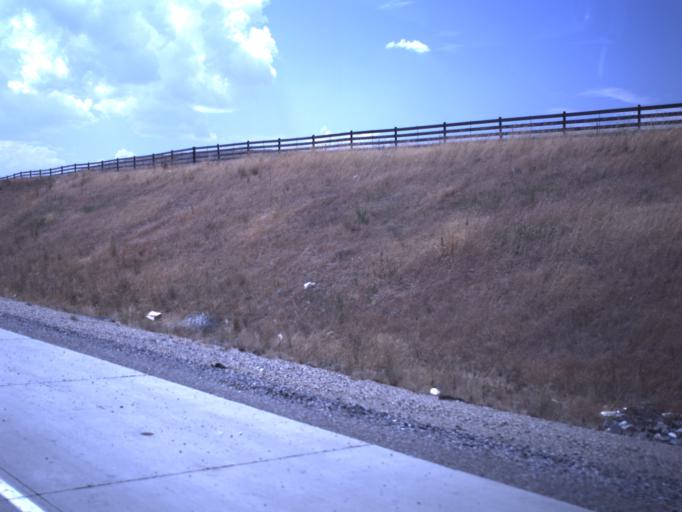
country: US
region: Utah
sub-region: Salt Lake County
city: Oquirrh
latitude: 40.6447
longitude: -112.0454
